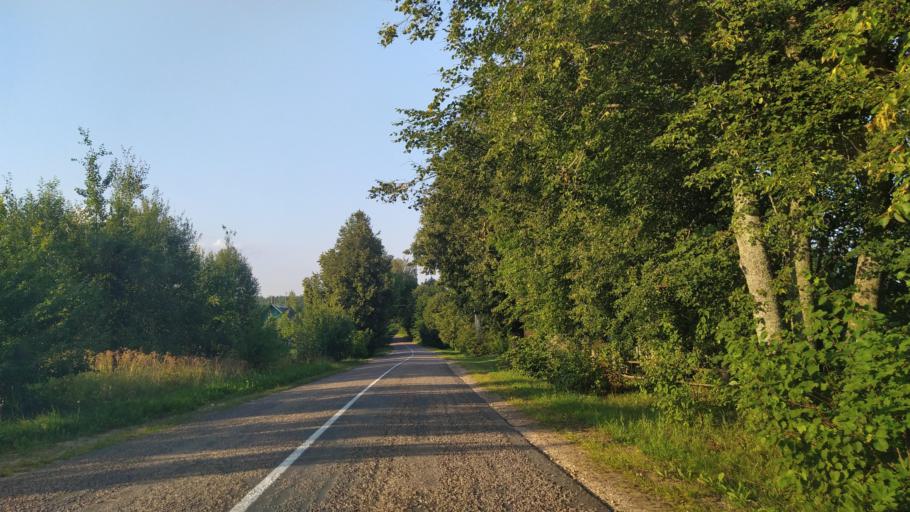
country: RU
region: Pskov
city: Pushkinskiye Gory
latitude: 57.0419
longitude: 28.9148
